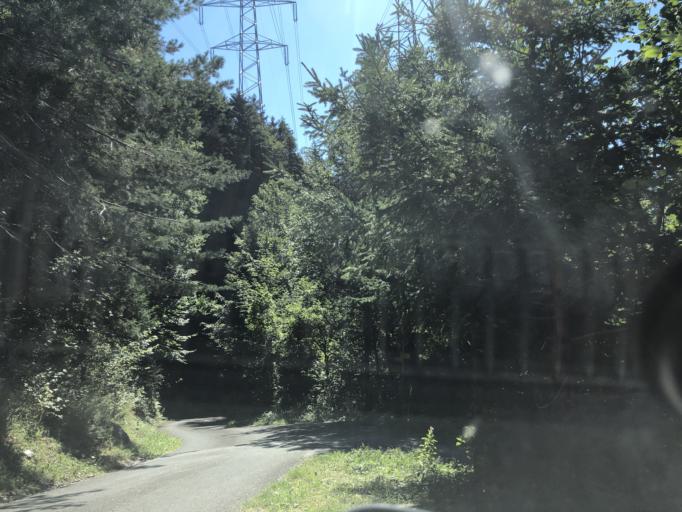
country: CH
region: Uri
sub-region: Uri
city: Flueelen
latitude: 46.9081
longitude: 8.6343
